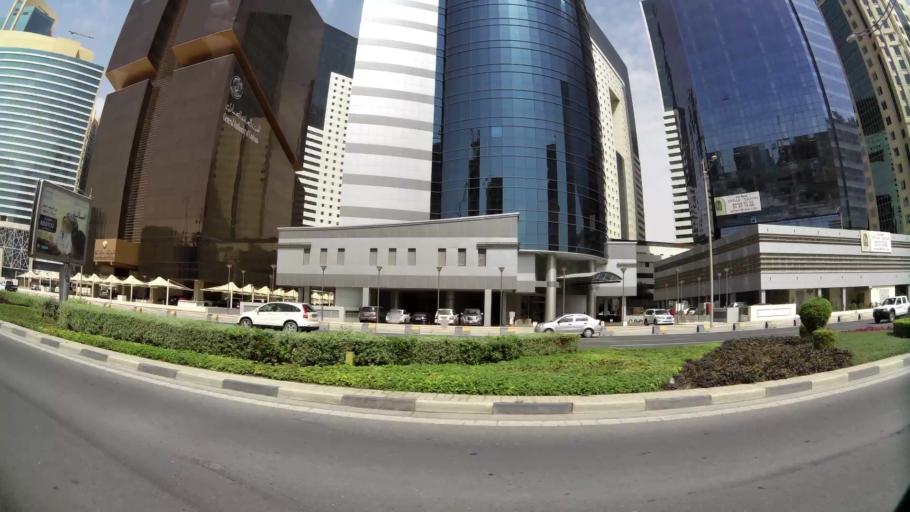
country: QA
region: Baladiyat ad Dawhah
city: Doha
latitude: 25.3172
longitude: 51.5226
